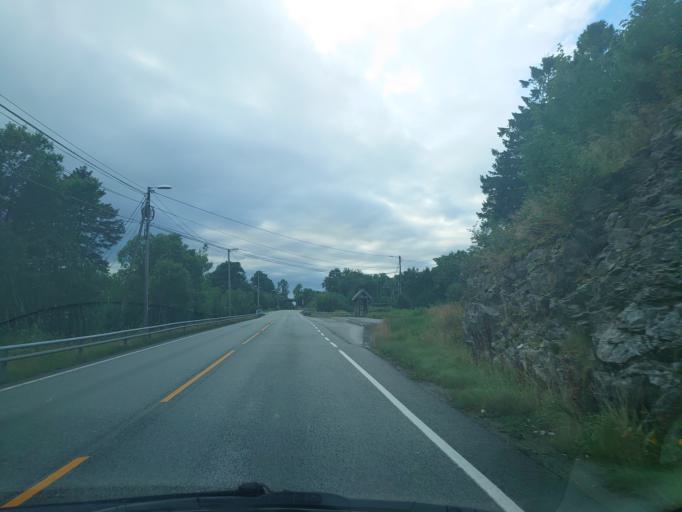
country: NO
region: Hordaland
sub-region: Lindas
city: Isdalsto
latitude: 60.5652
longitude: 5.2444
